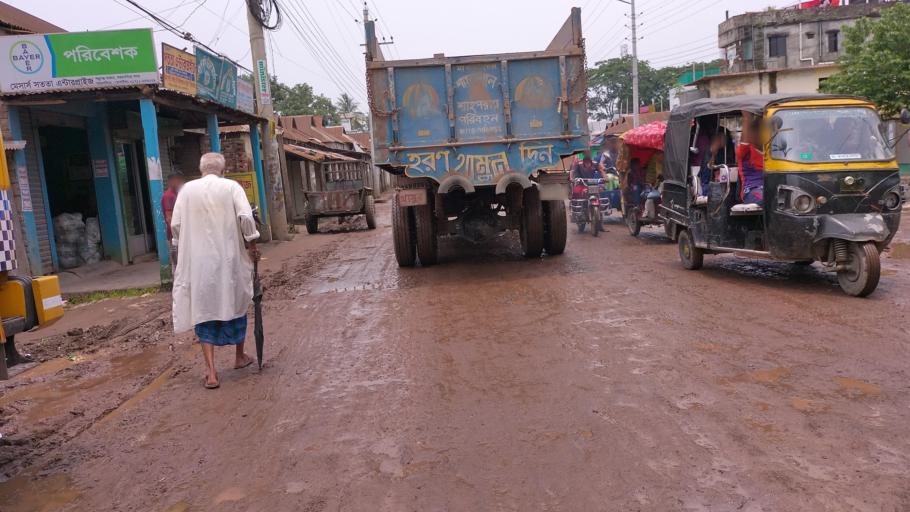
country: BD
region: Dhaka
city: Mymensingh
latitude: 24.7639
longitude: 90.4514
